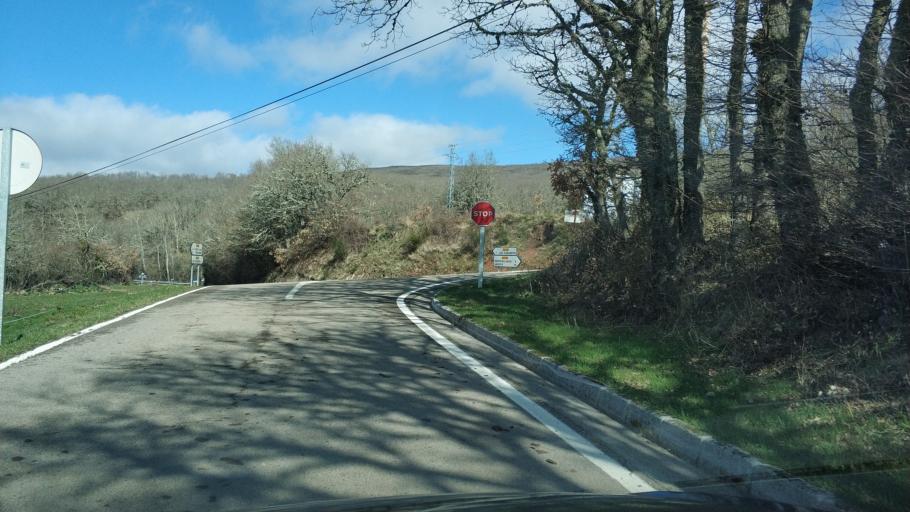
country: ES
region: Cantabria
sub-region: Provincia de Cantabria
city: Mataporquera
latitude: 42.9065
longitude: -4.0601
